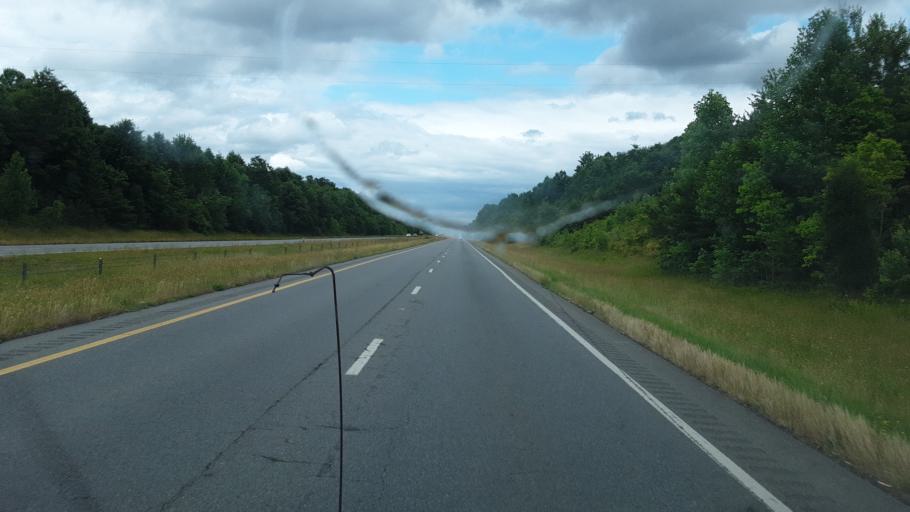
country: US
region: North Carolina
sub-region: Yadkin County
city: Yadkinville
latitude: 36.1196
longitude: -80.6886
